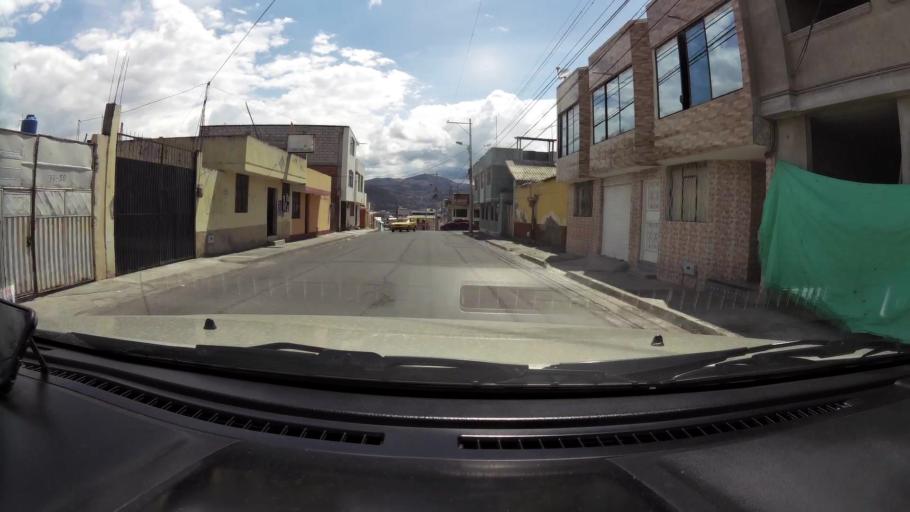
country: EC
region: Chimborazo
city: Riobamba
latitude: -1.6607
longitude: -78.6459
